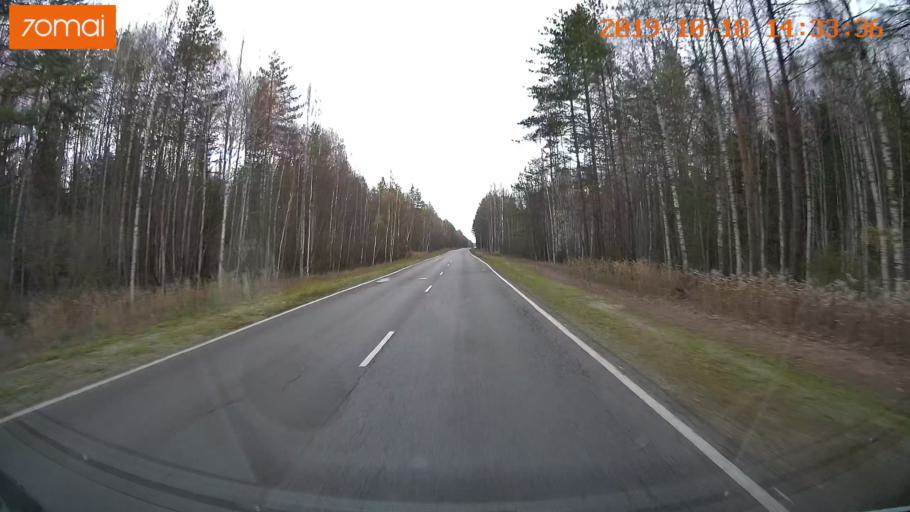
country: RU
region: Rjazan
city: Tuma
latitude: 55.2033
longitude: 40.6000
